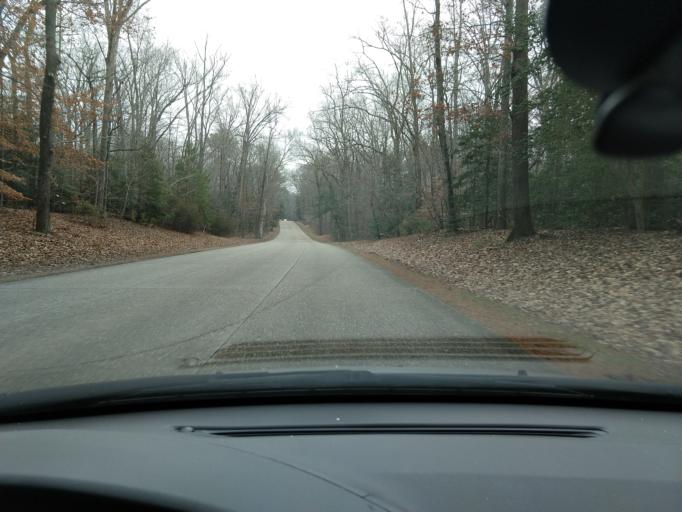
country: US
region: Virginia
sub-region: City of Williamsburg
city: Williamsburg
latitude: 37.2817
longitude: -76.6316
